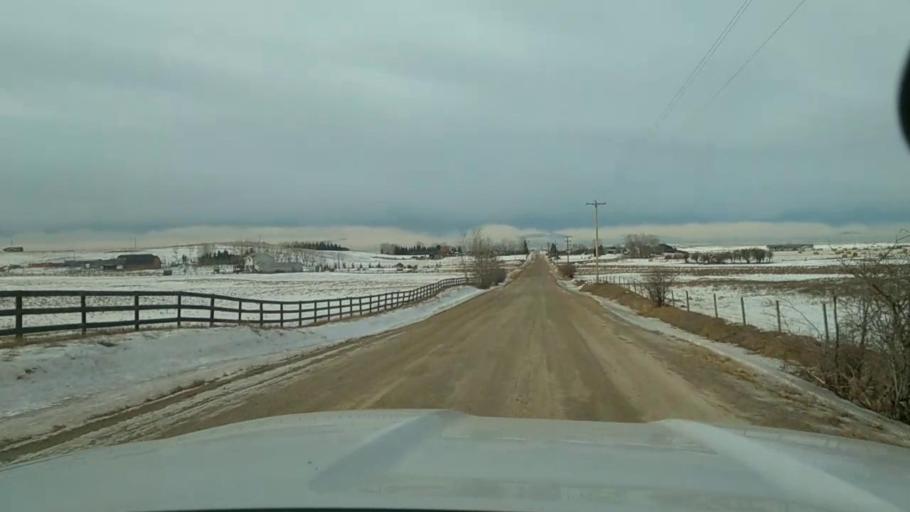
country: CA
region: Alberta
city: Airdrie
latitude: 51.2417
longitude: -113.9250
